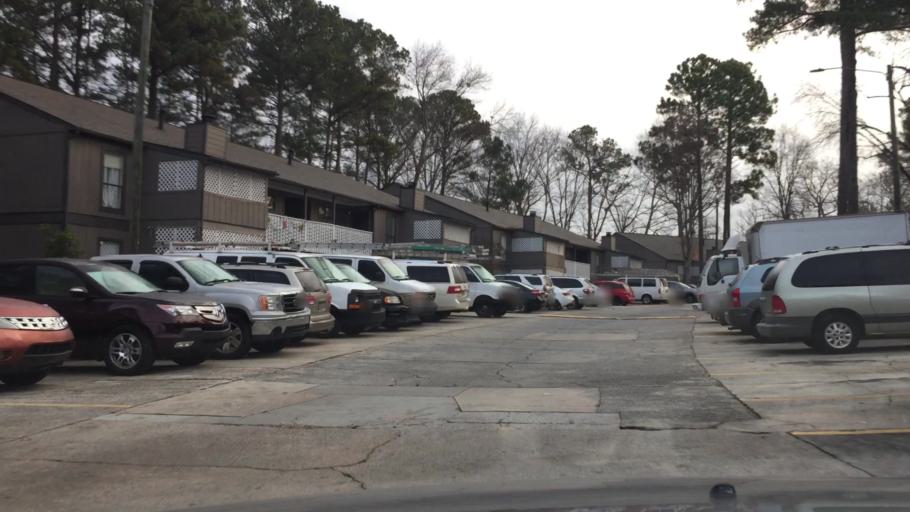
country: US
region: Georgia
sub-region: DeKalb County
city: Doraville
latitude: 33.9394
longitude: -84.2713
